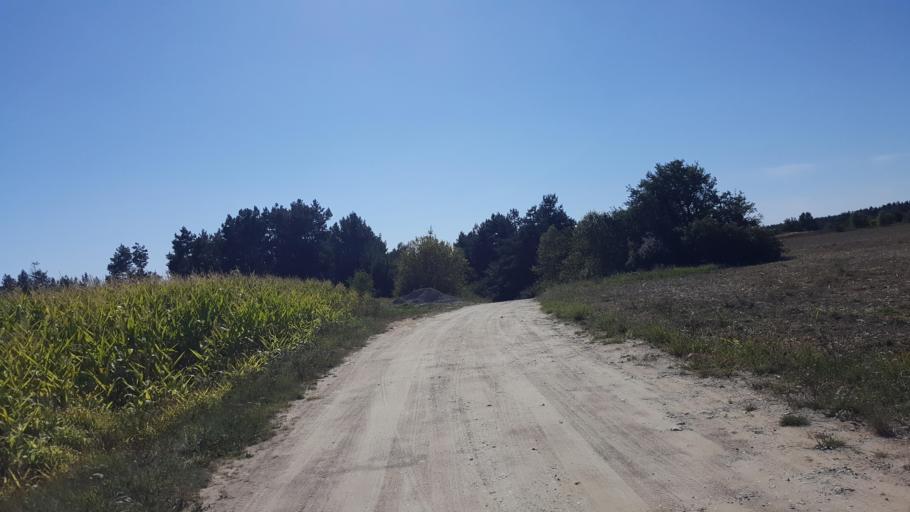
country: PL
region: Lublin Voivodeship
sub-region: Powiat bialski
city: Rokitno
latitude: 52.2291
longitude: 23.3218
